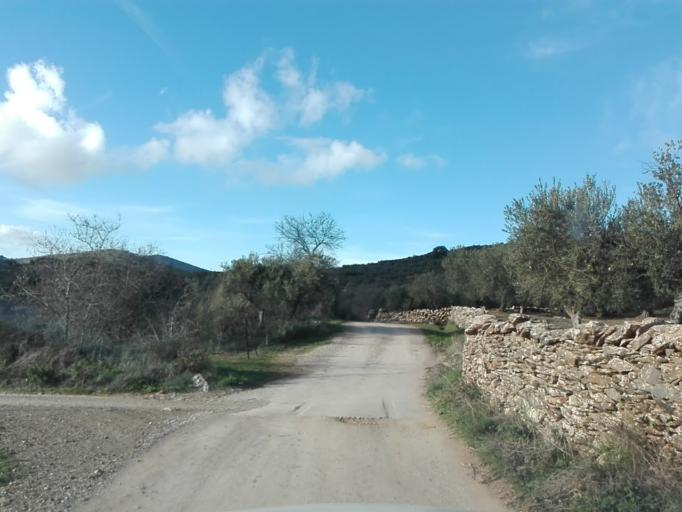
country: ES
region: Extremadura
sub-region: Provincia de Badajoz
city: Trasierra
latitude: 38.1953
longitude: -5.9867
